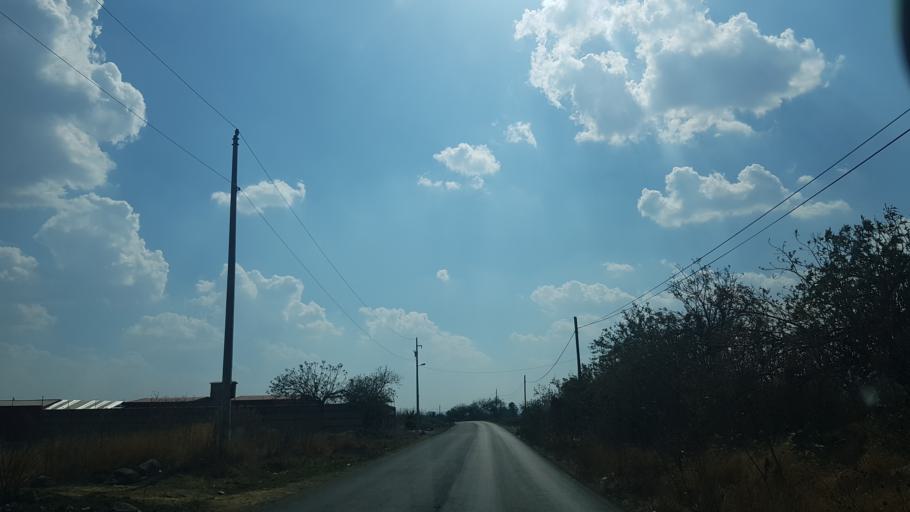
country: MX
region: Puebla
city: Atlixco
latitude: 18.9077
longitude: -98.4773
